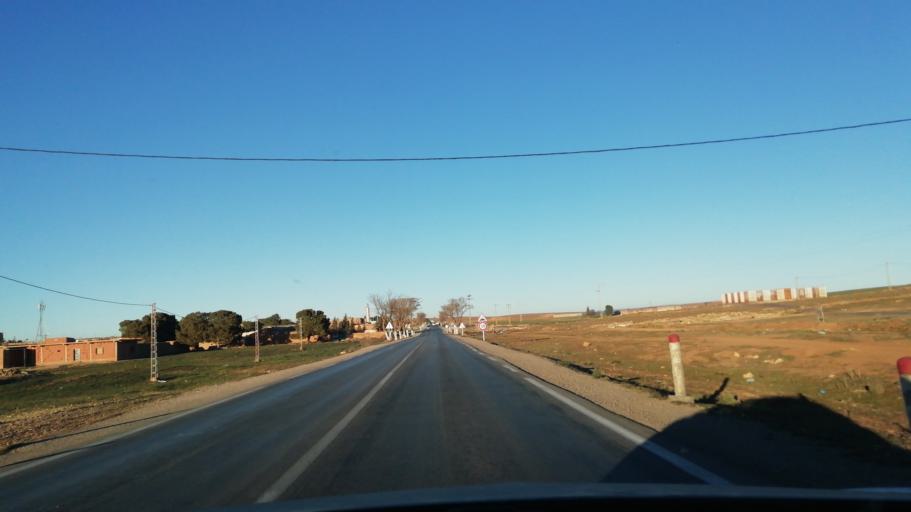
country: DZ
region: Saida
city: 'Ain el Hadjar
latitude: 34.5760
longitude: 0.1281
